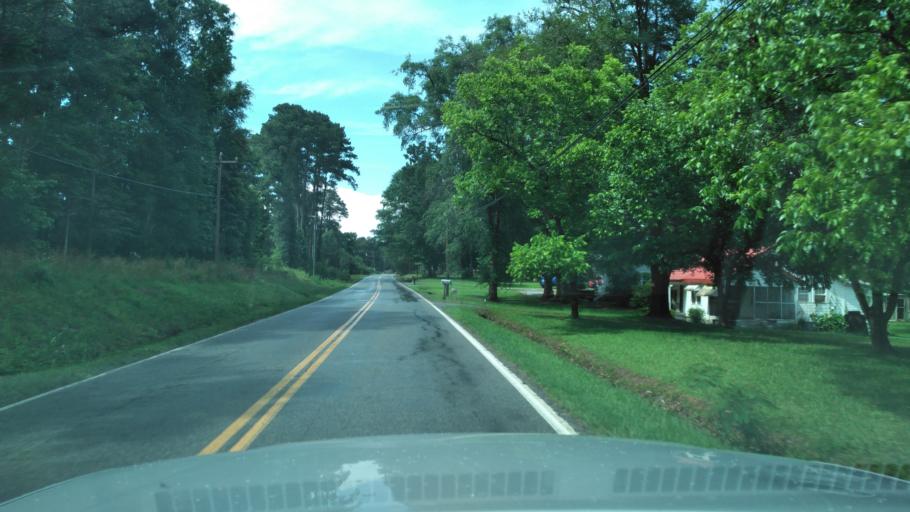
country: US
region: South Carolina
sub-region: Spartanburg County
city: Woodruff
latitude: 34.7261
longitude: -82.0454
